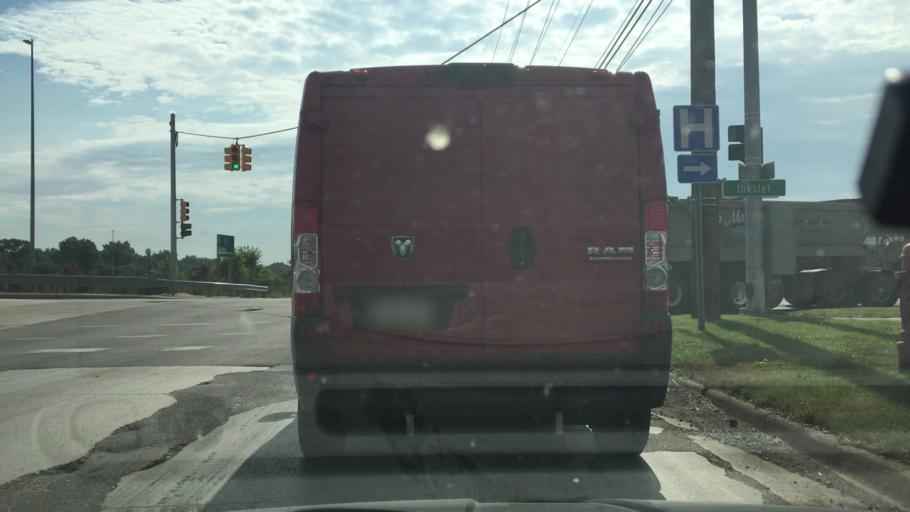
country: US
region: Michigan
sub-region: Wayne County
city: Redford
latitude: 42.3836
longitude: -83.3146
